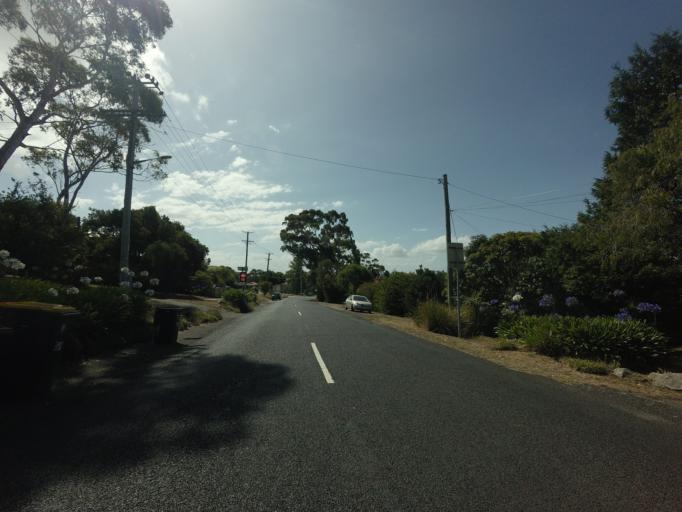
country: AU
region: Tasmania
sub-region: Hobart
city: Dynnyrne
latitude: -42.9151
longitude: 147.3239
